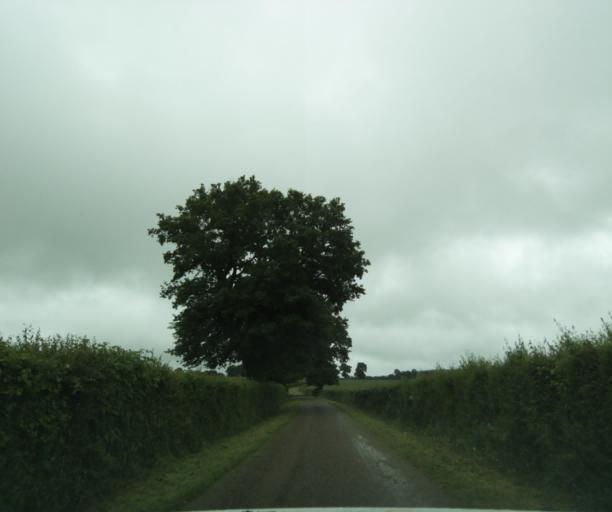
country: FR
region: Bourgogne
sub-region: Departement de Saone-et-Loire
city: Charolles
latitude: 46.4303
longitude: 4.3240
